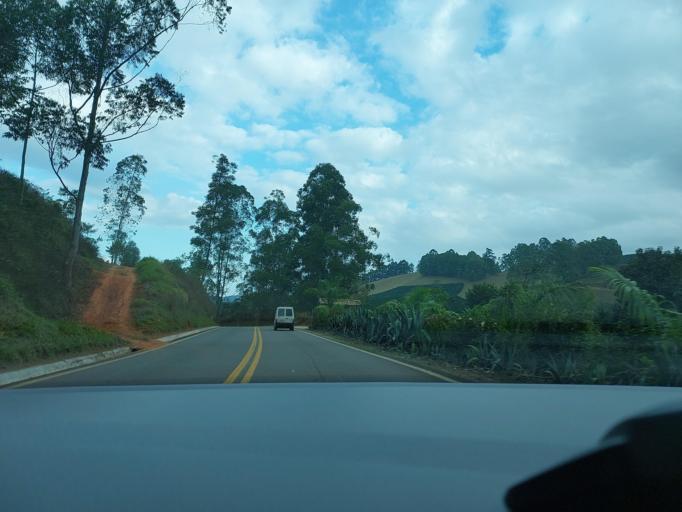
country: BR
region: Minas Gerais
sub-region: Mirai
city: Mirai
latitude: -21.0253
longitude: -42.5414
